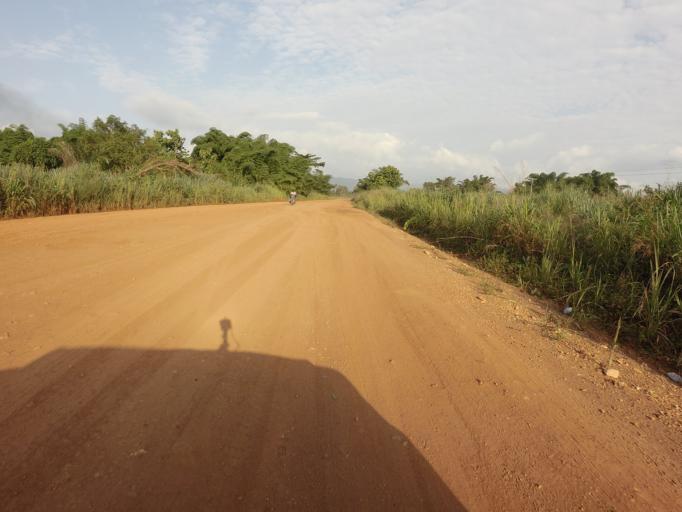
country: GH
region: Volta
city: Kpandu
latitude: 6.9882
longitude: 0.4429
